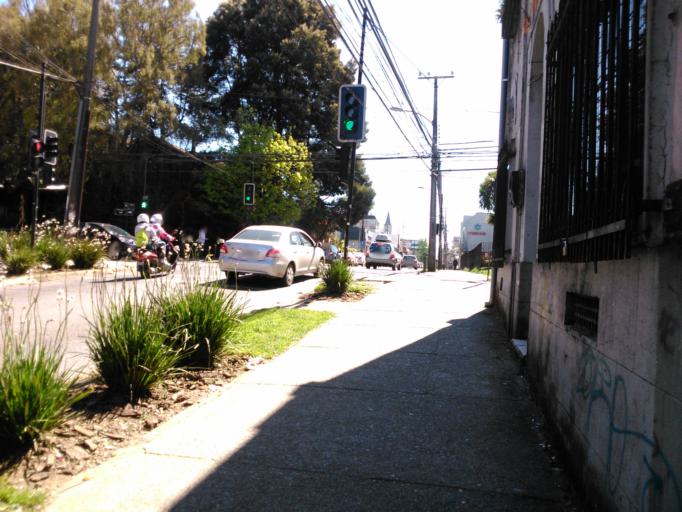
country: CL
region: Los Rios
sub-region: Provincia de Valdivia
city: Valdivia
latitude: -39.8181
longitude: -73.2473
